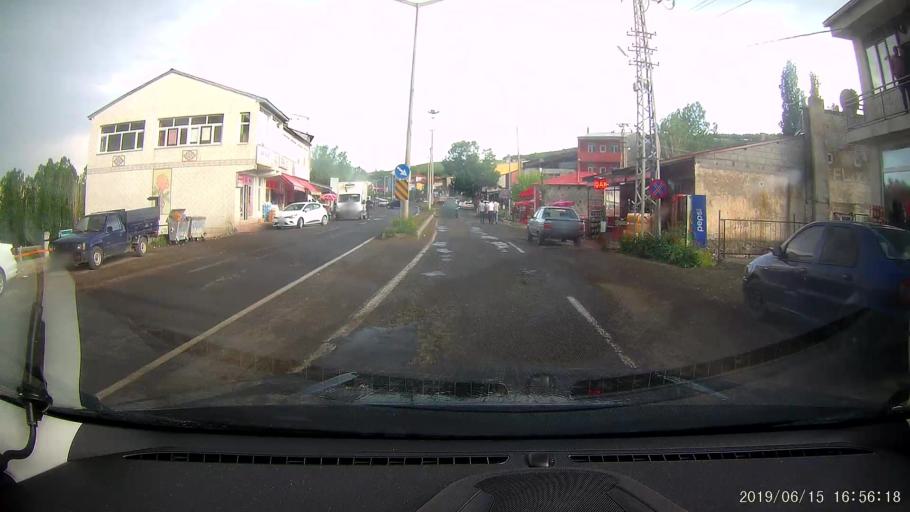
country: TR
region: Kars
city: Susuz
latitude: 40.7806
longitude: 43.1271
